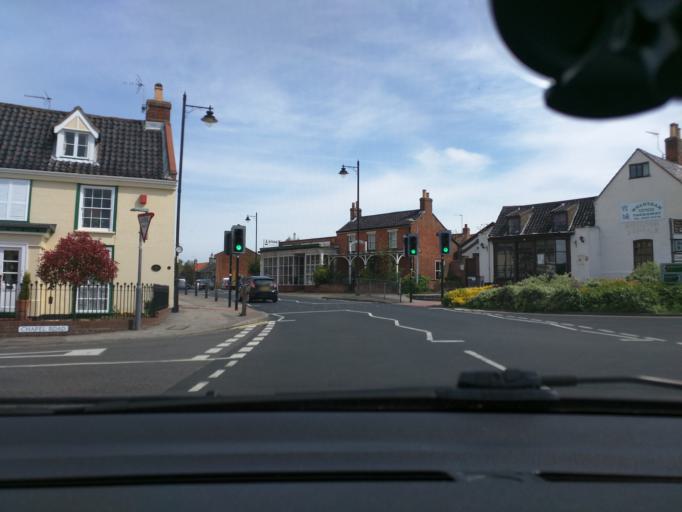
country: GB
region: England
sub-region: Suffolk
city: Wrentham
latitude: 52.3847
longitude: 1.6701
